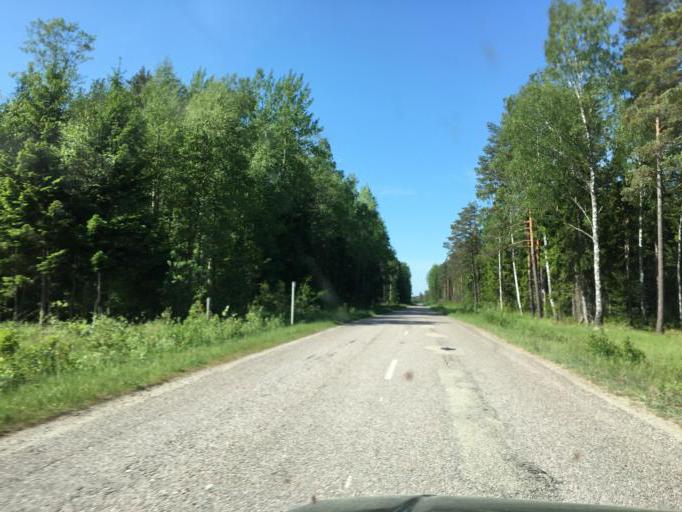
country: LV
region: Ventspils
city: Ventspils
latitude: 57.4884
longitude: 21.7847
